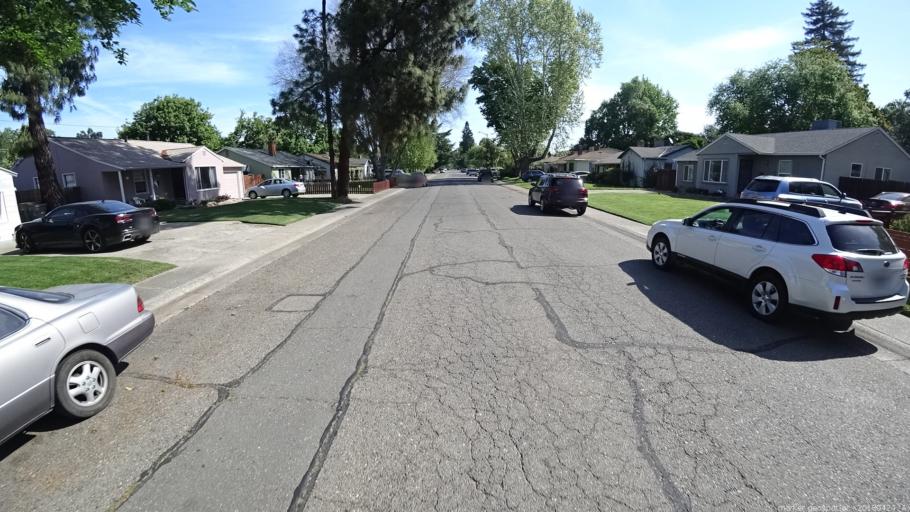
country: US
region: California
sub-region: Yolo County
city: West Sacramento
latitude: 38.5643
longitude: -121.5351
